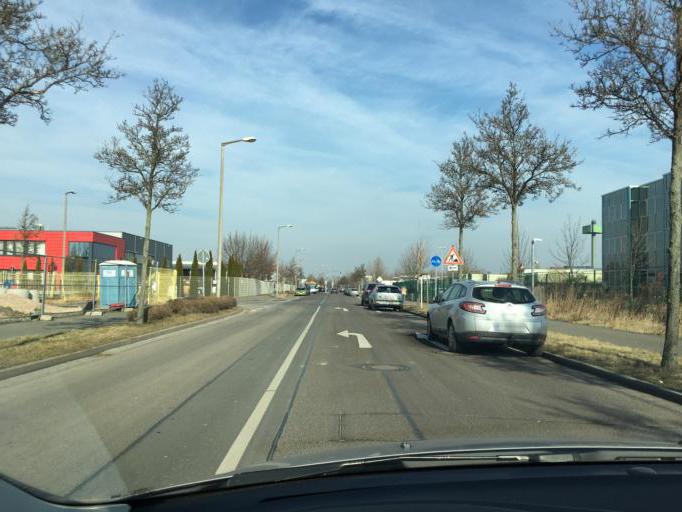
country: DE
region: Saxony
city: Taucha
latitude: 51.3638
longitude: 12.4383
